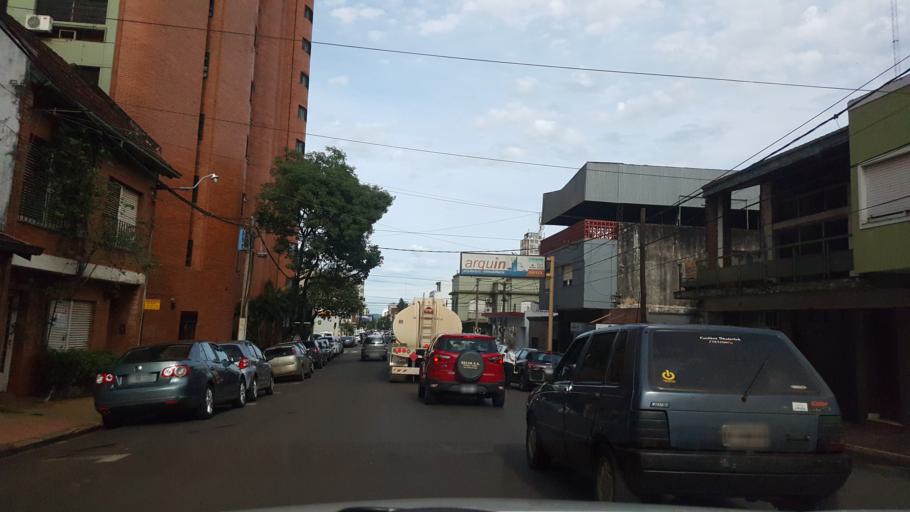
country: AR
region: Misiones
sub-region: Departamento de Capital
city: Posadas
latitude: -27.3711
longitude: -55.8992
